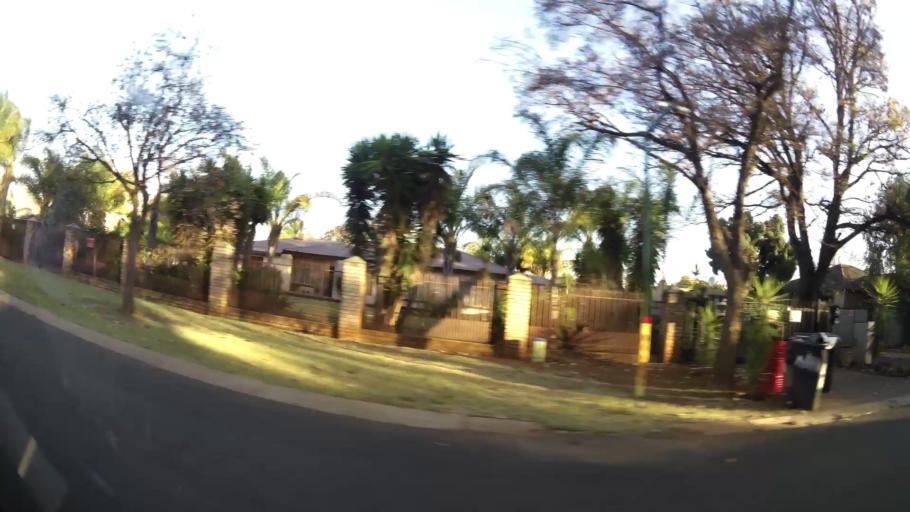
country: ZA
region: Gauteng
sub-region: City of Tshwane Metropolitan Municipality
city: Pretoria
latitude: -25.7049
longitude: 28.2637
